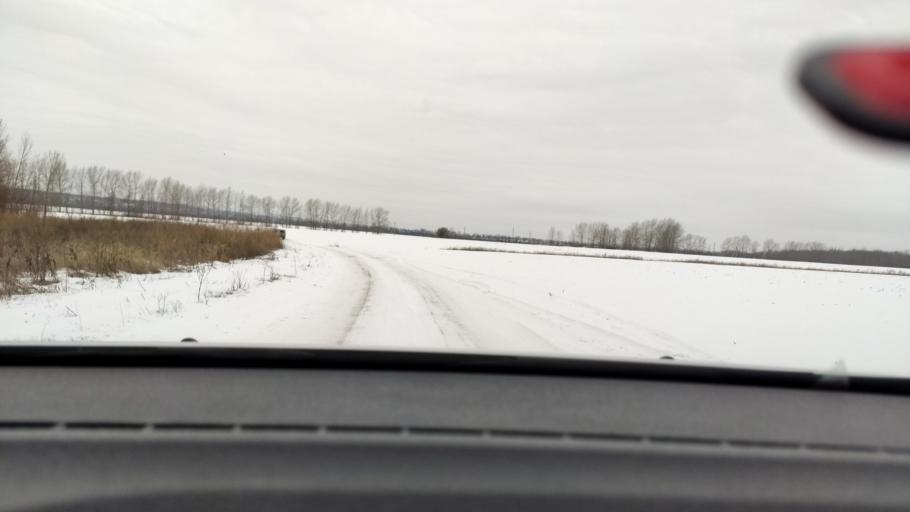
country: RU
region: Voronezj
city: Semiluki
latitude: 51.7142
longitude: 38.9832
